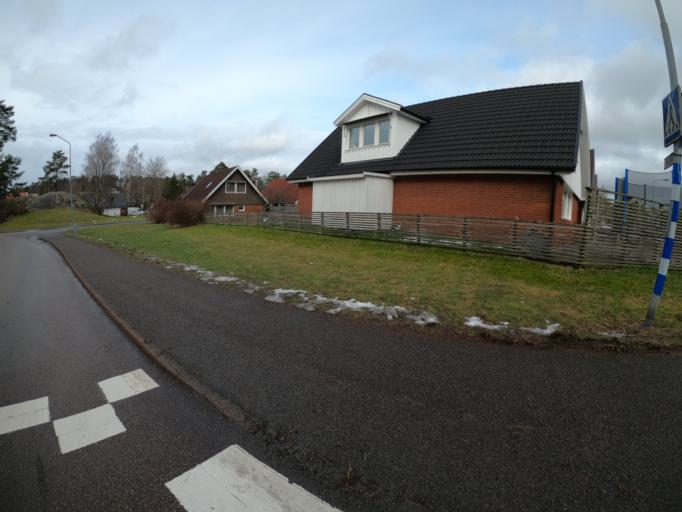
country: SE
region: Vaestra Goetaland
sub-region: Harryda Kommun
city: Molnlycke
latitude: 57.6487
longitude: 12.1189
